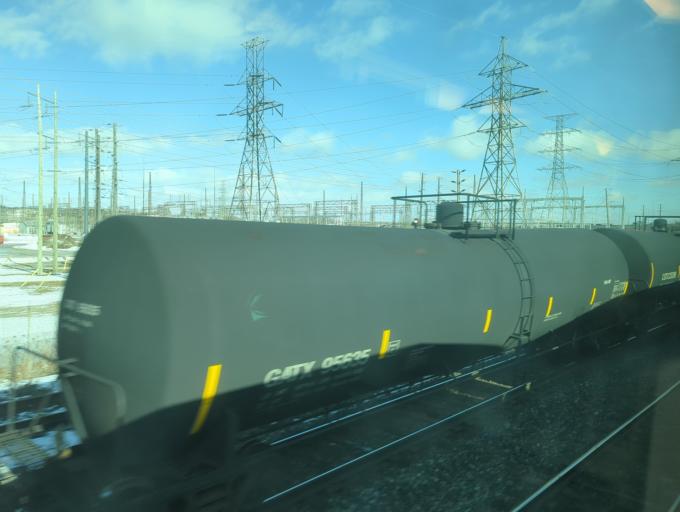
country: CA
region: Ontario
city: Burlington
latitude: 43.3279
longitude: -79.8306
